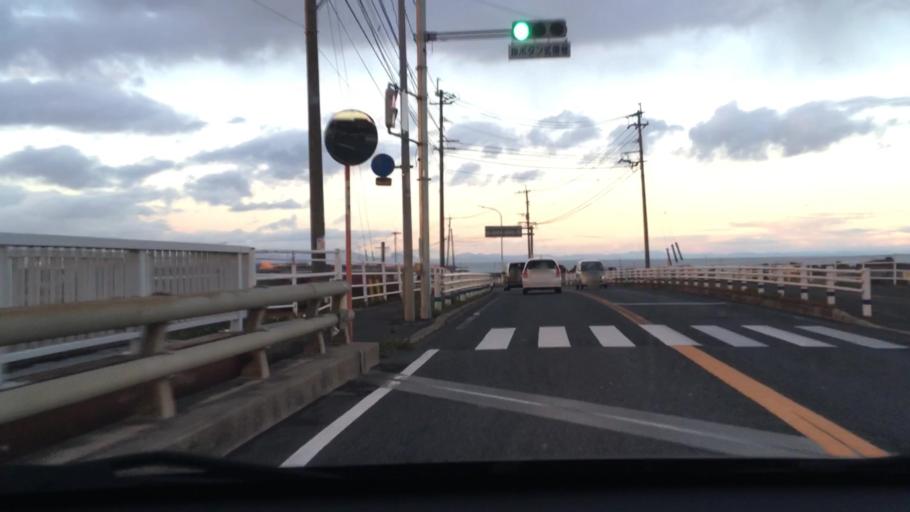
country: JP
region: Fukuoka
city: Shiida
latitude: 33.6269
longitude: 131.0880
